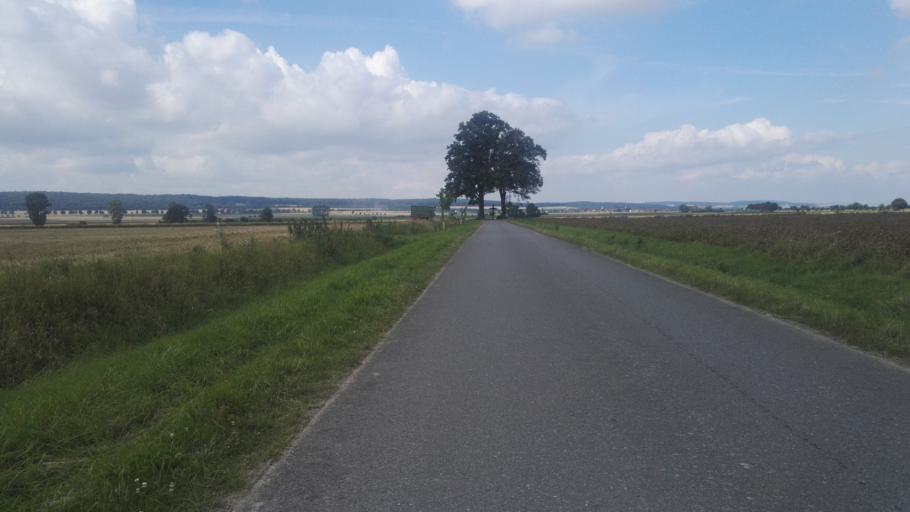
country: DE
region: Lower Saxony
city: Schellerten
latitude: 52.1587
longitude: 10.0536
